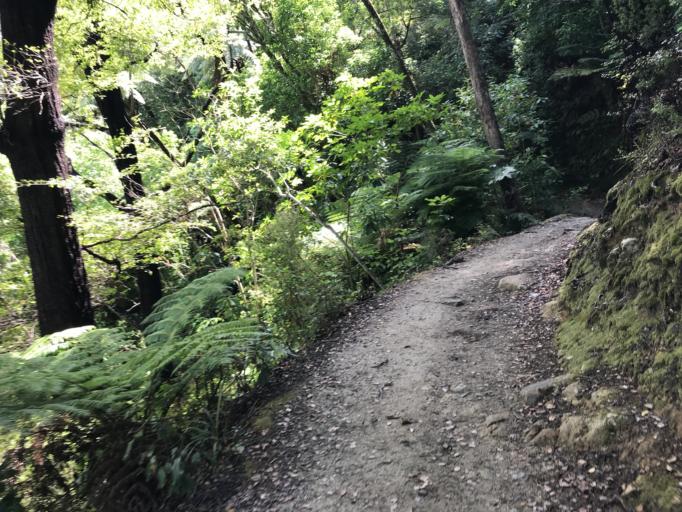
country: NZ
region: Marlborough
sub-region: Marlborough District
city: Picton
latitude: -41.2583
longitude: 173.9365
